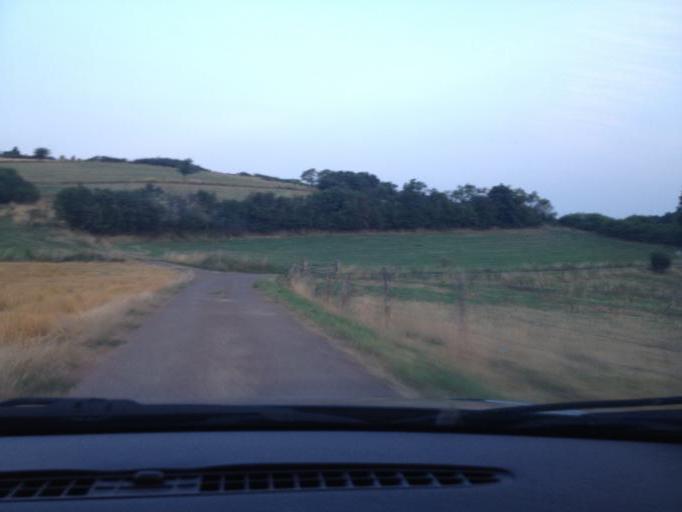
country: DE
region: Saarland
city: Namborn
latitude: 49.5447
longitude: 7.1503
